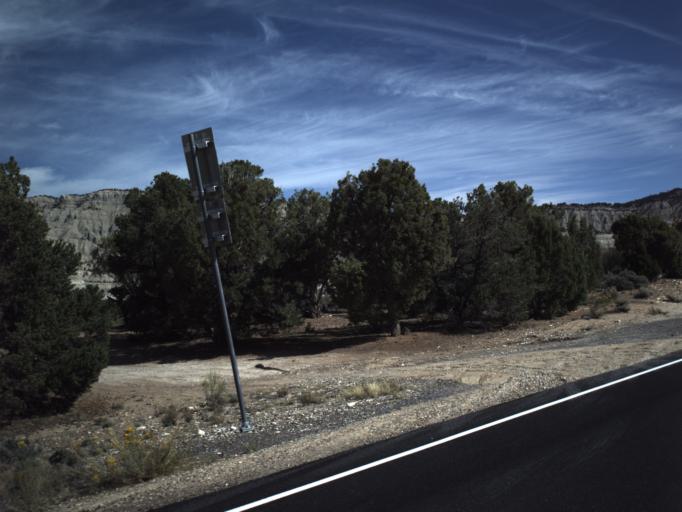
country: US
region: Utah
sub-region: Garfield County
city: Panguitch
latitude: 37.6209
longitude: -111.8706
